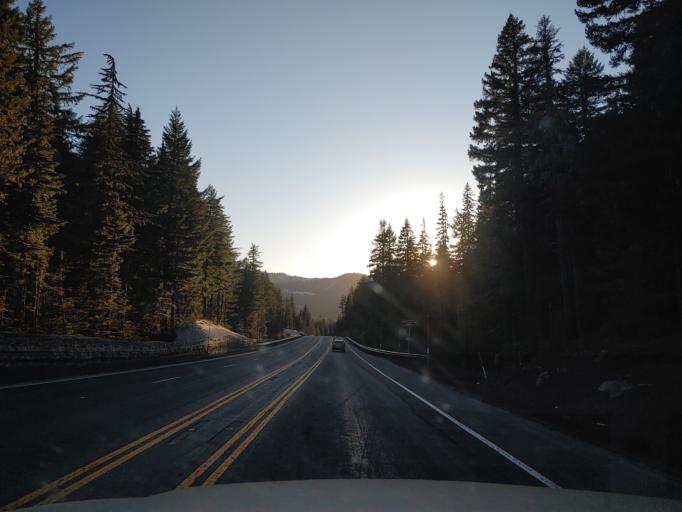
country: US
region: Oregon
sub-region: Lane County
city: Oakridge
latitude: 43.6113
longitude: -122.1128
